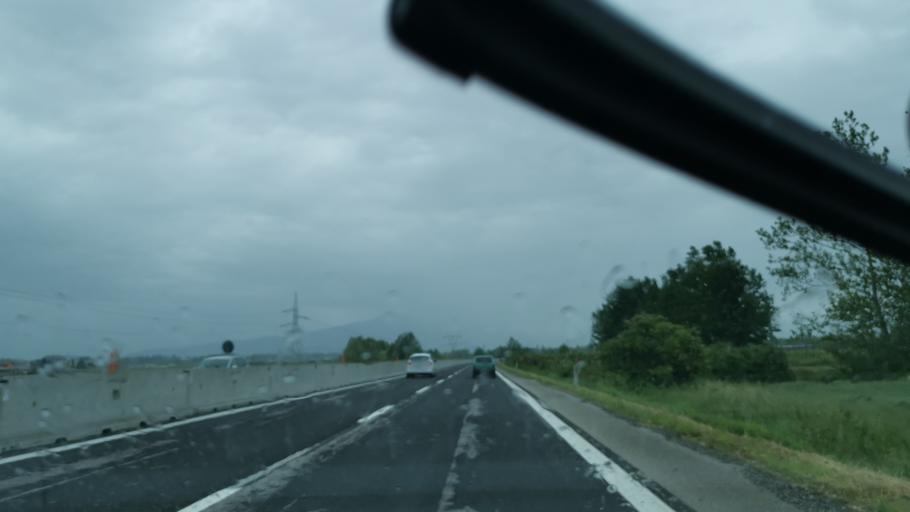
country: IT
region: Veneto
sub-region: Provincia di Verona
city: Castelnuovo del Garda
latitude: 45.4504
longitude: 10.7489
